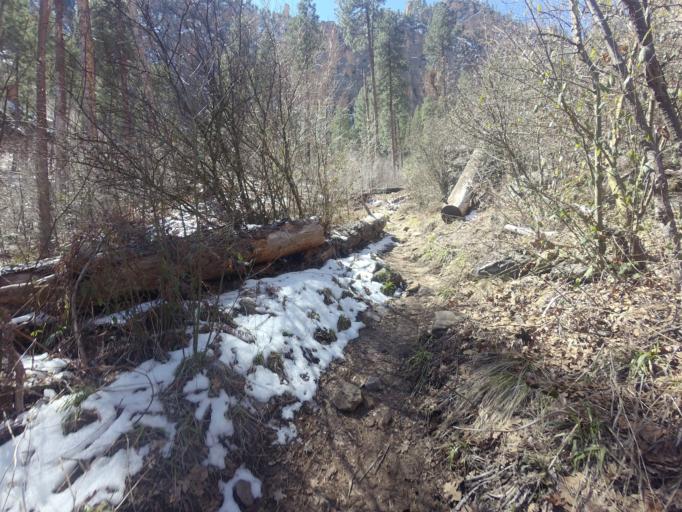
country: US
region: Arizona
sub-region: Coconino County
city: Sedona
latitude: 34.9335
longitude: -111.7551
